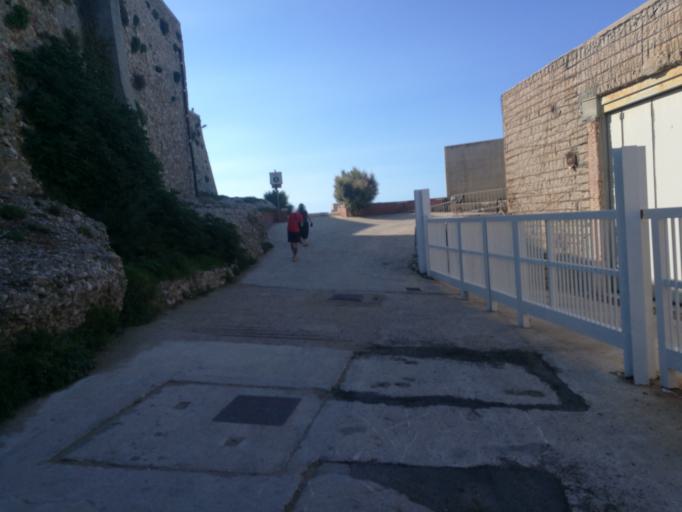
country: IT
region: Molise
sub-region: Provincia di Campobasso
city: Termoli
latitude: 42.0055
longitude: 14.9984
